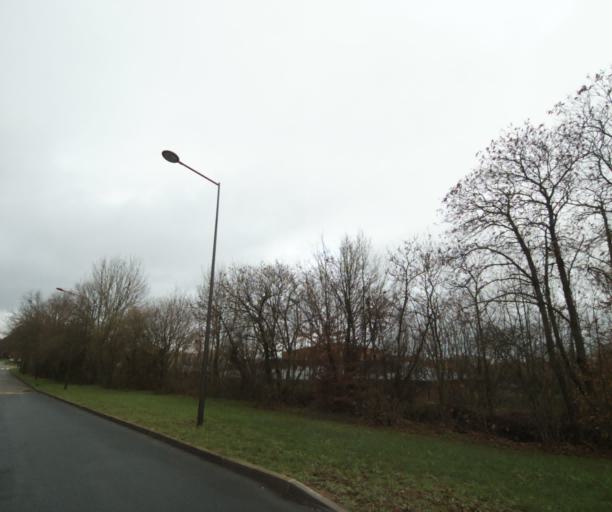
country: FR
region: Pays de la Loire
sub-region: Departement de la Sarthe
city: Rouillon
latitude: 48.0187
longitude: 0.1463
